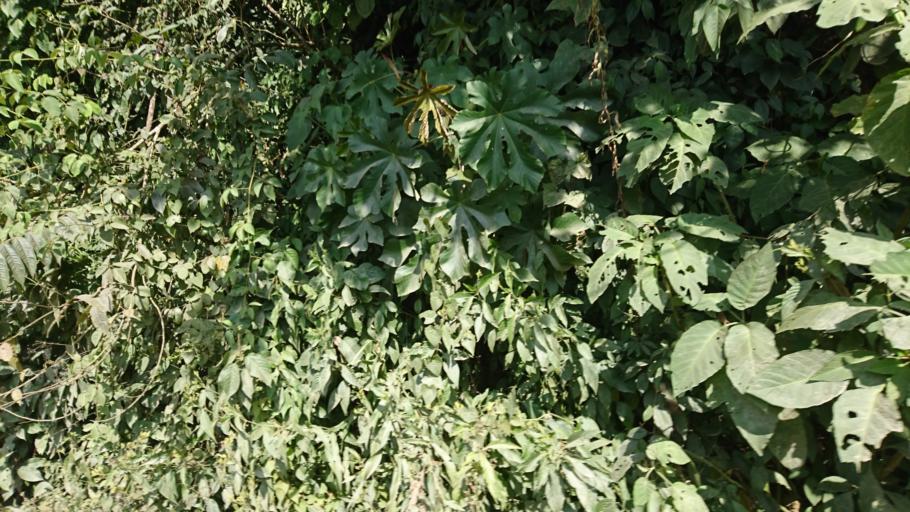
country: BO
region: La Paz
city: Coroico
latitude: -16.0875
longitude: -67.7853
